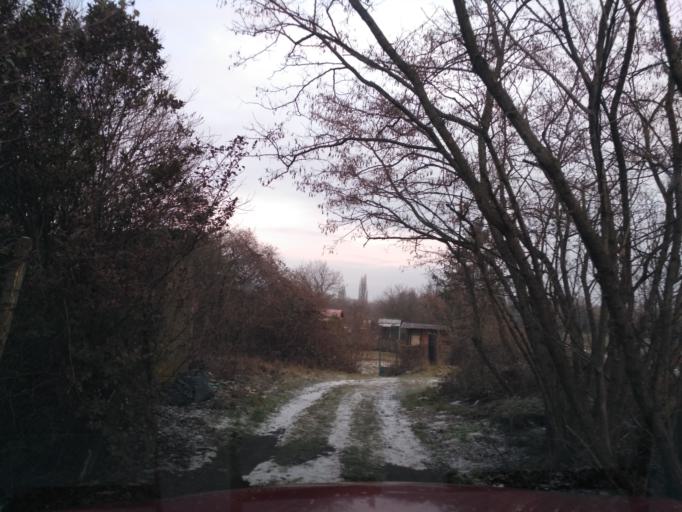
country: SK
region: Kosicky
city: Kosice
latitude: 48.7291
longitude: 21.2712
